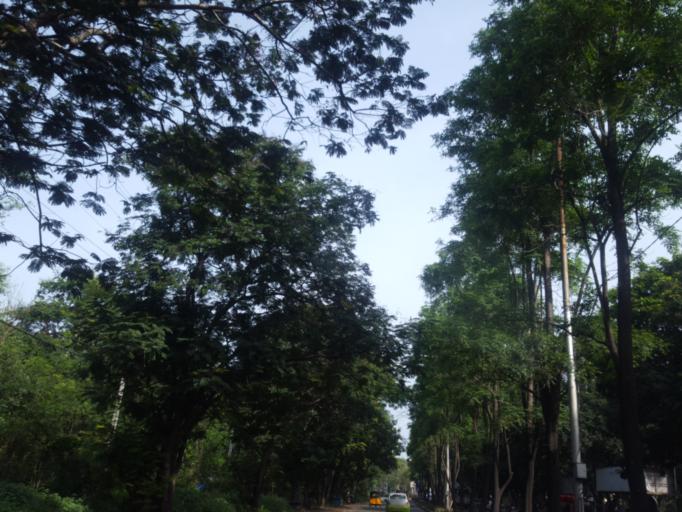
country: IN
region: Telangana
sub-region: Medak
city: Serilingampalle
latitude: 17.4589
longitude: 78.3382
